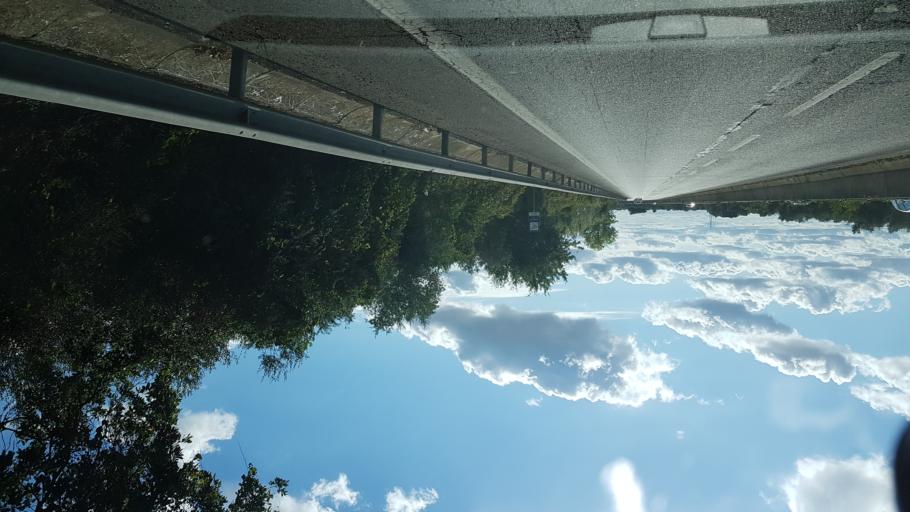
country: IT
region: Apulia
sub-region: Provincia di Brindisi
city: San Pietro Vernotico
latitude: 40.5155
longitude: 18.0210
